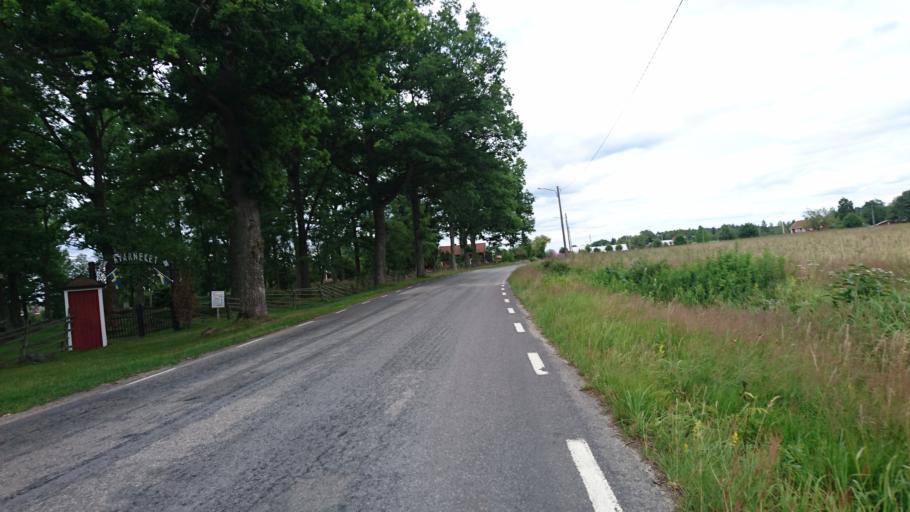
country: SE
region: Kronoberg
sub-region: Alvesta Kommun
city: Moheda
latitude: 56.9841
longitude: 14.5825
